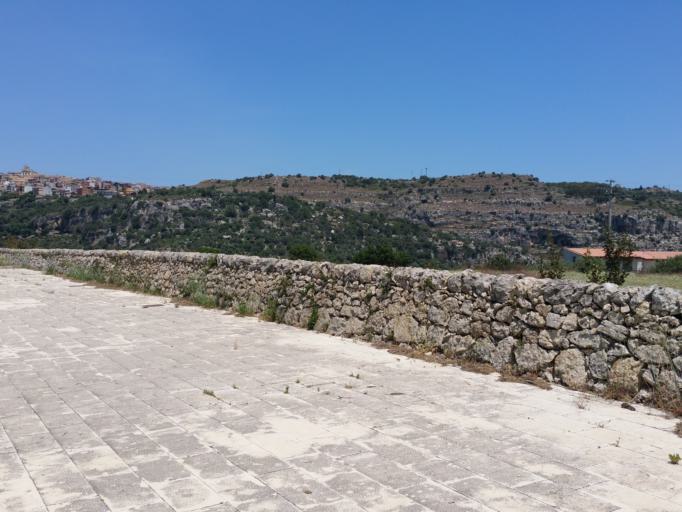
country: IT
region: Sicily
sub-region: Provincia di Siracusa
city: Sortino
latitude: 37.1450
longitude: 15.0335
